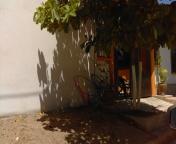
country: MX
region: Oaxaca
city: Asuncion Ixtaltepec
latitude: 16.5000
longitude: -95.0609
